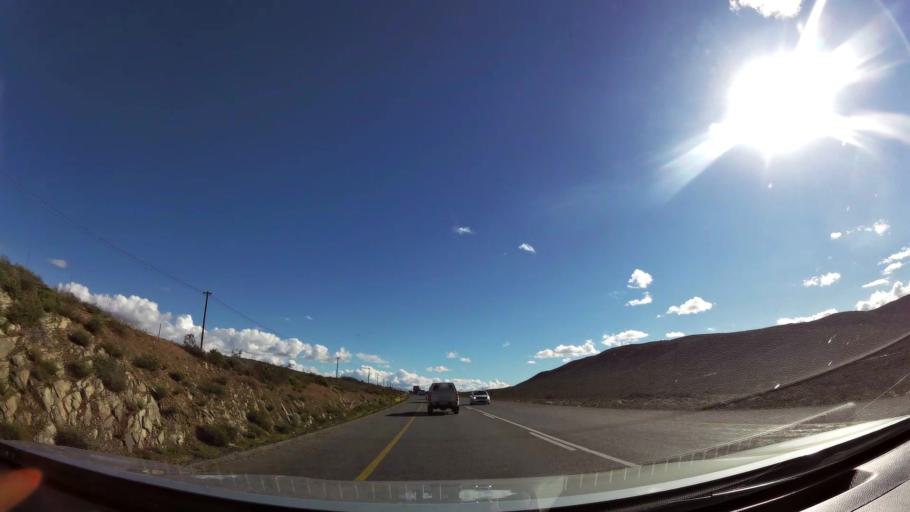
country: ZA
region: Western Cape
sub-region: Cape Winelands District Municipality
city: Worcester
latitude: -33.7347
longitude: 19.6685
